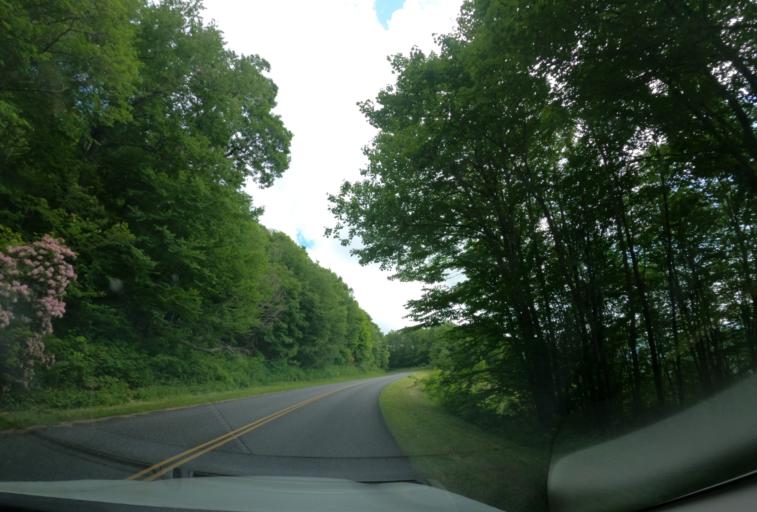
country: US
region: North Carolina
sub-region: Haywood County
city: Hazelwood
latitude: 35.4162
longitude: -83.0412
